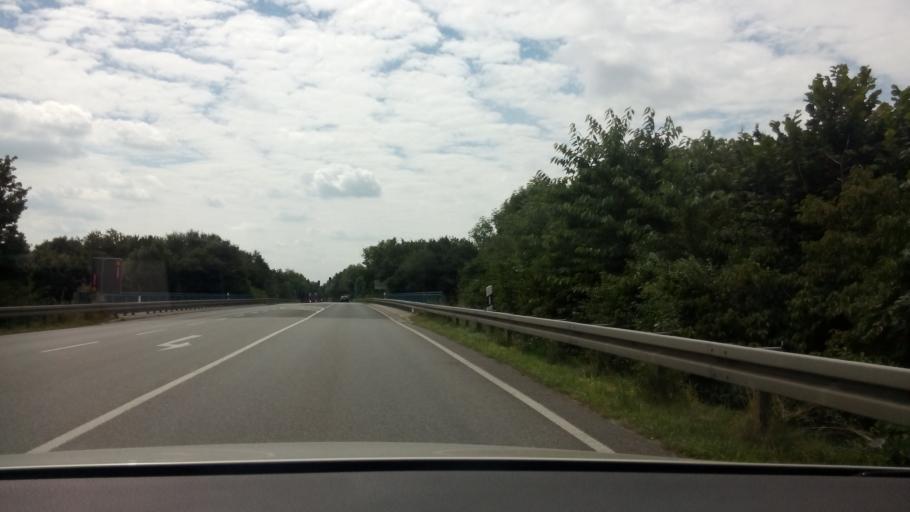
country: DE
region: Bavaria
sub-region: Upper Bavaria
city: Marzling
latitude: 48.3880
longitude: 11.7786
